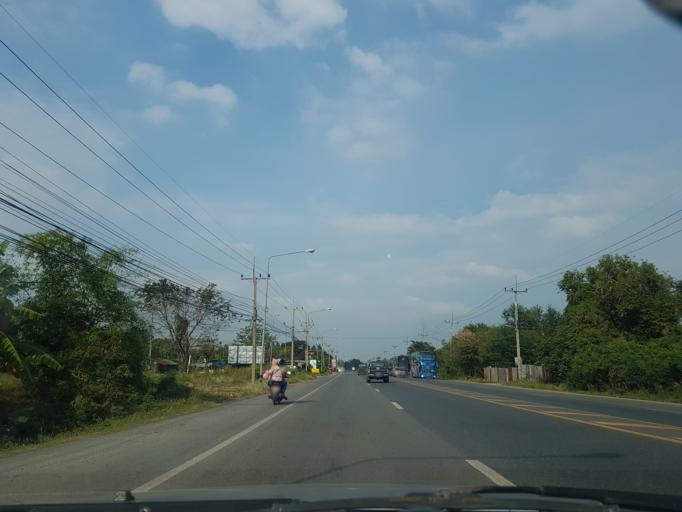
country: TH
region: Sara Buri
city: Ban Mo
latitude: 14.5956
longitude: 100.7334
